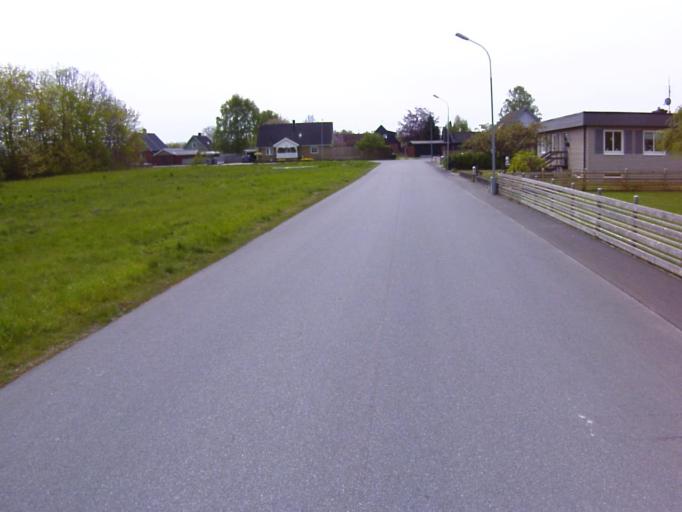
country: SE
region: Skane
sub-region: Kristianstads Kommun
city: Onnestad
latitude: 55.9362
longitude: 13.9884
